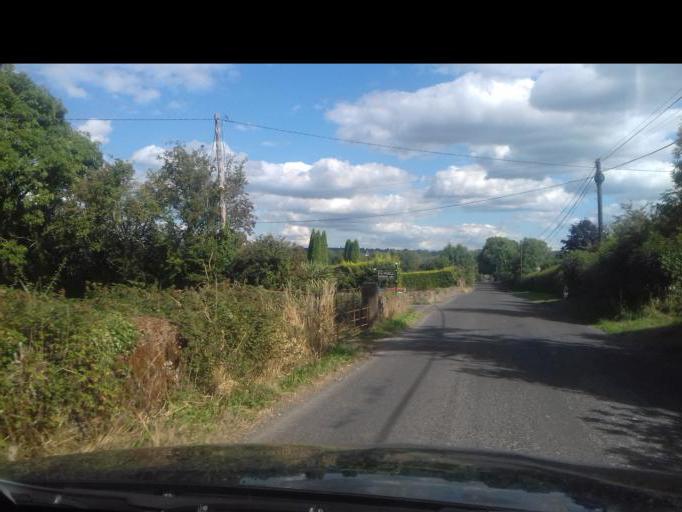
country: IE
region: Leinster
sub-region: Kilkenny
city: Thomastown
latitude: 52.5153
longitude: -7.1802
